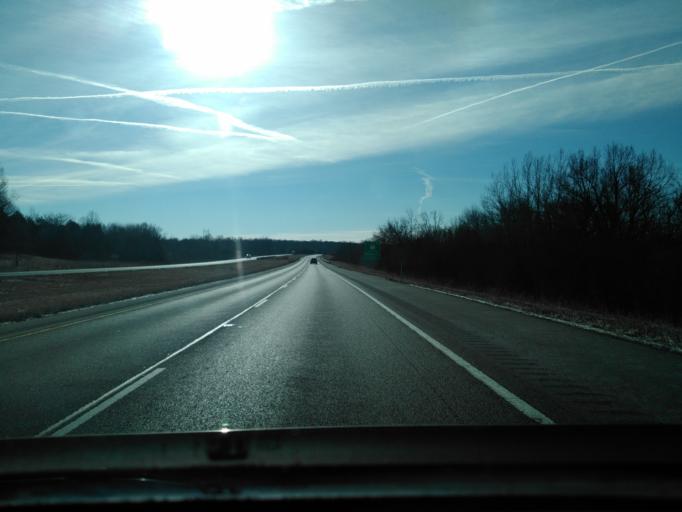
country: US
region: Illinois
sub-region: Johnson County
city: Vienna
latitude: 37.4336
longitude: -88.8824
